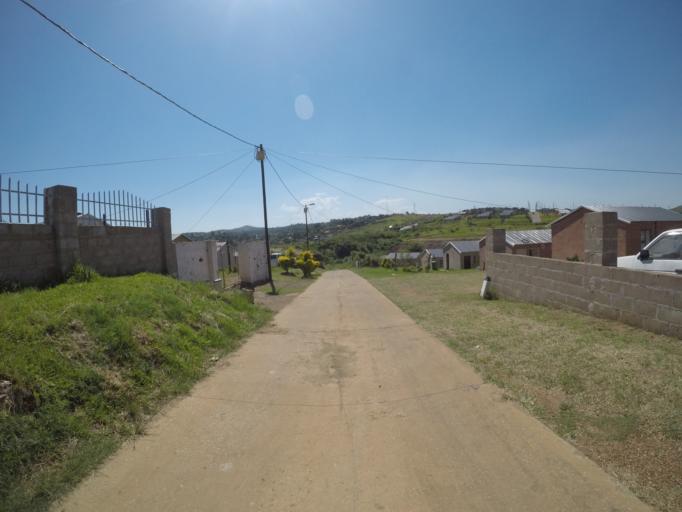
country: ZA
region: KwaZulu-Natal
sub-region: uThungulu District Municipality
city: Empangeni
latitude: -28.7667
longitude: 31.8772
